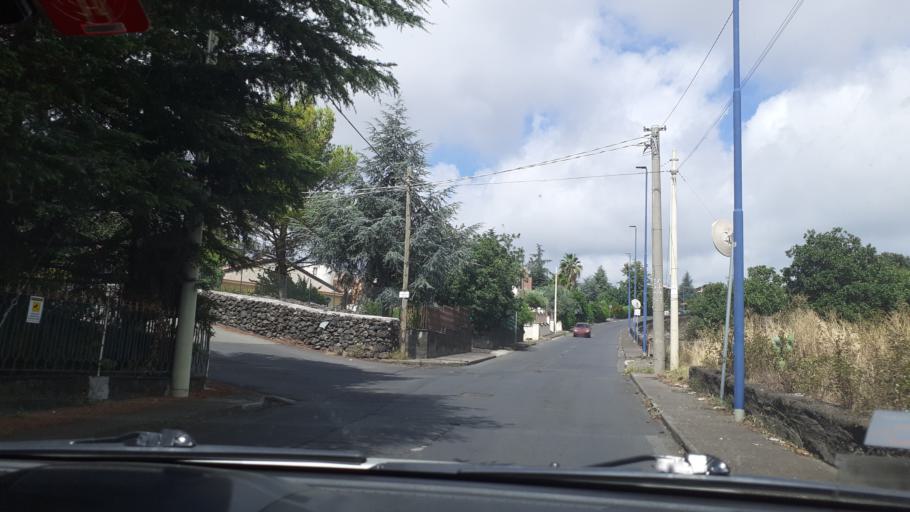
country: IT
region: Sicily
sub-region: Catania
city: Pedara
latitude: 37.6087
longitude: 15.0593
